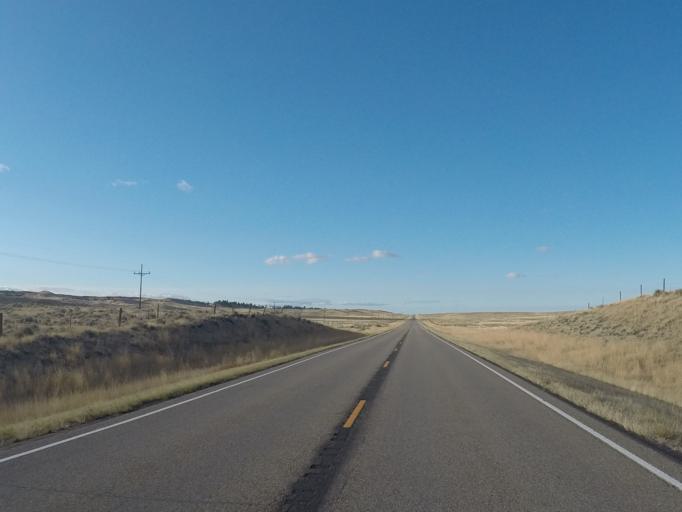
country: US
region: Montana
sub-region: Golden Valley County
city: Ryegate
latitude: 46.2219
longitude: -108.9279
